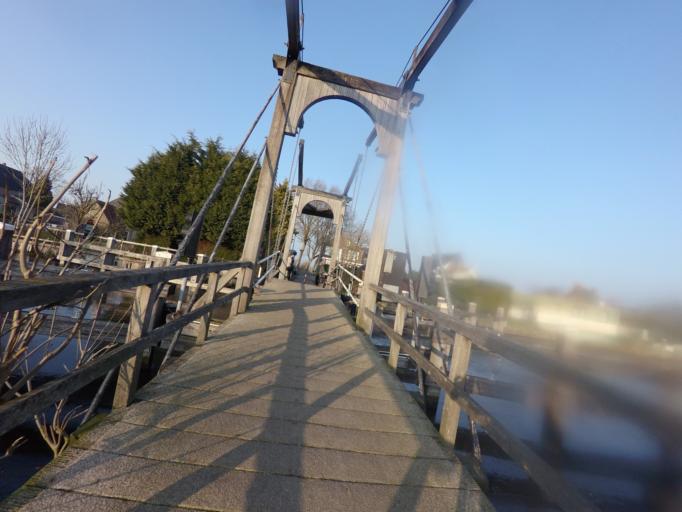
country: NL
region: South Holland
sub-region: Gemeente Vlist
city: Vlist
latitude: 52.0139
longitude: 4.8112
